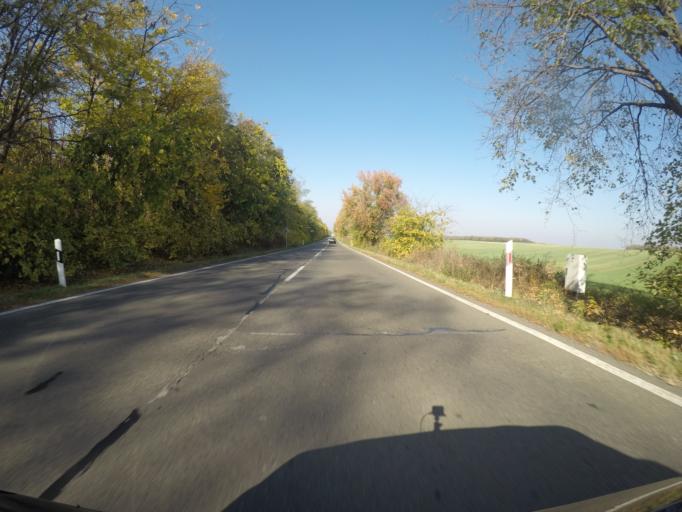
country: HU
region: Tolna
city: Szedres
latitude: 46.5181
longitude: 18.6624
